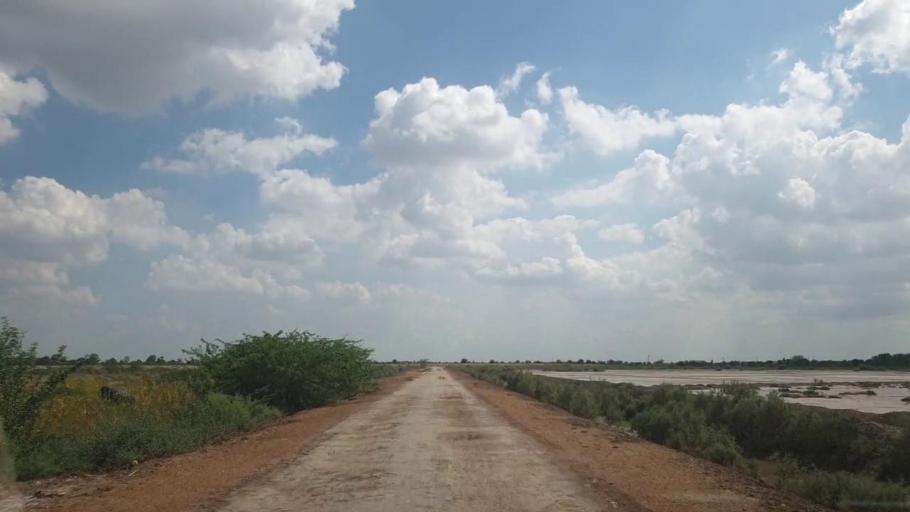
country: PK
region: Sindh
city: Pithoro
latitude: 25.5958
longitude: 69.4017
